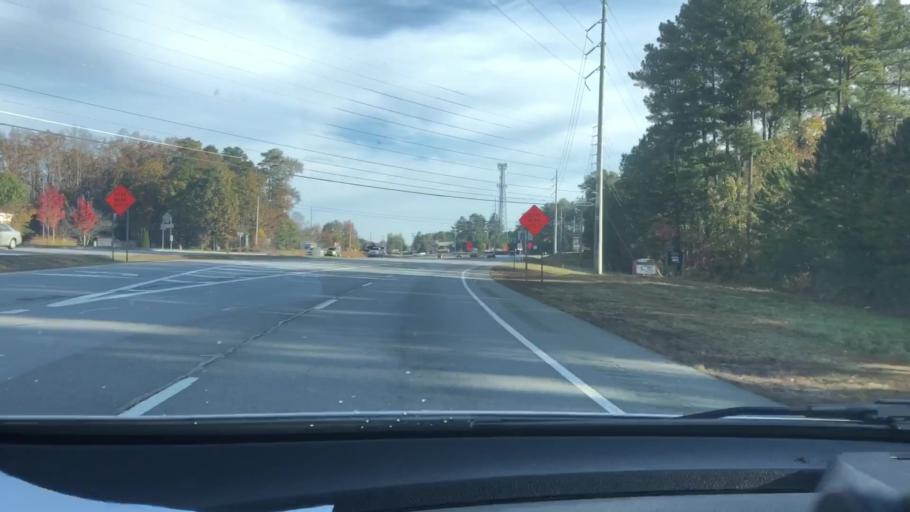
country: US
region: Georgia
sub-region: Fulton County
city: Johns Creek
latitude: 34.1175
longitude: -84.1753
